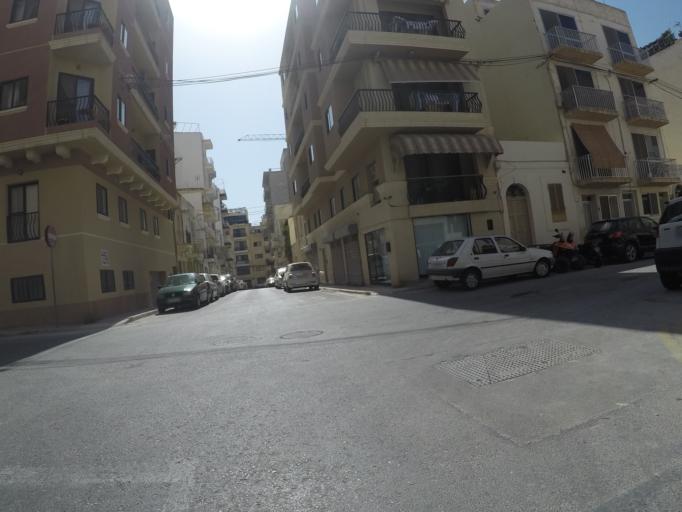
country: MT
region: Saint Paul's Bay
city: San Pawl il-Bahar
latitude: 35.9491
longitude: 14.4095
